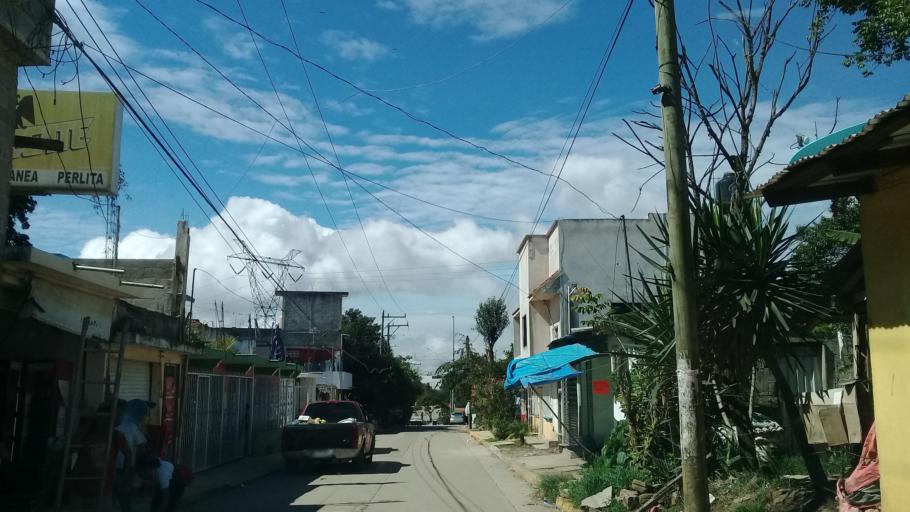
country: MX
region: Veracruz
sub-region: Jilotepec
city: El Pueblito (Garbanzal)
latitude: 19.5758
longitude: -96.9030
